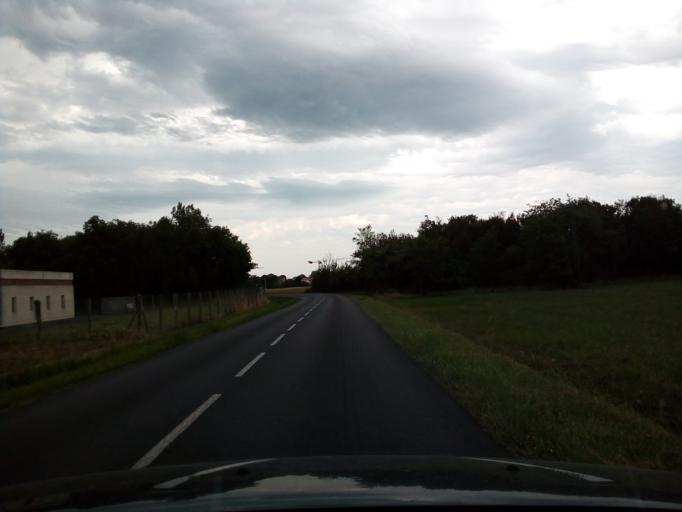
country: FR
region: Poitou-Charentes
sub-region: Departement de la Charente-Maritime
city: Dolus-d'Oleron
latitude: 45.9349
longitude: -1.3124
